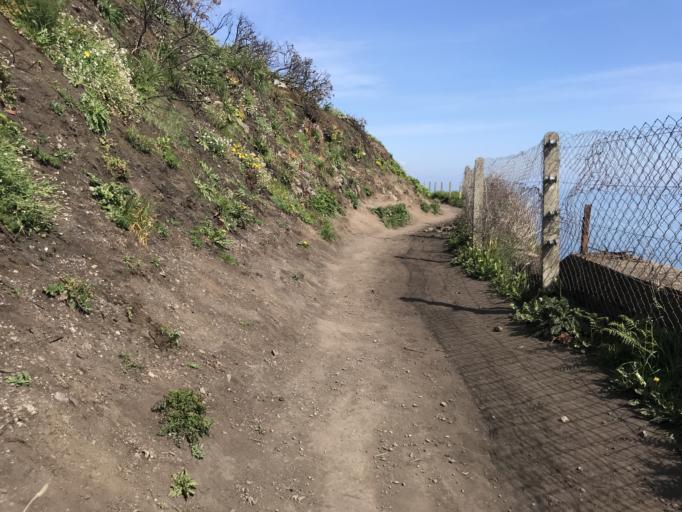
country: IE
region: Leinster
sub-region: Wicklow
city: Bray
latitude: 53.1804
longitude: -6.0758
